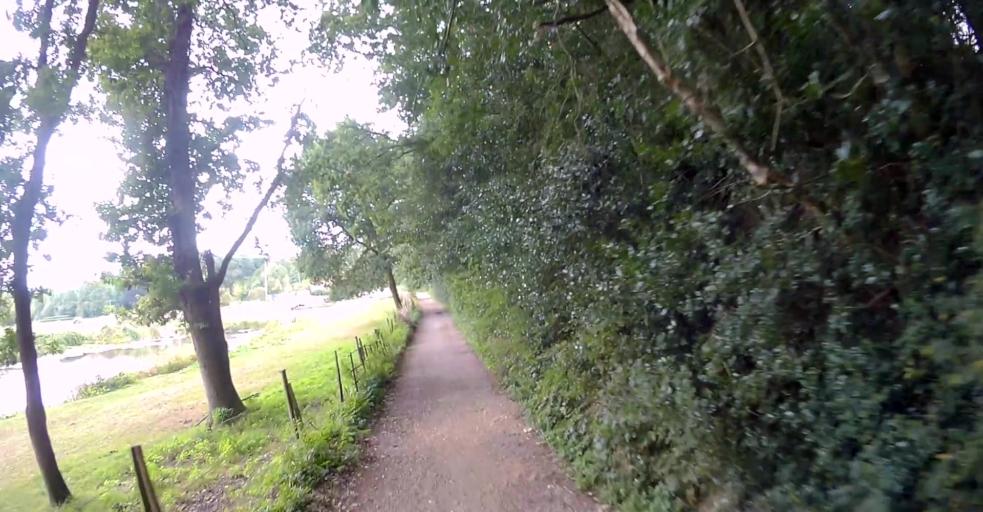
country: GB
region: England
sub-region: Surrey
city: Hale
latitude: 51.2160
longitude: -0.7702
